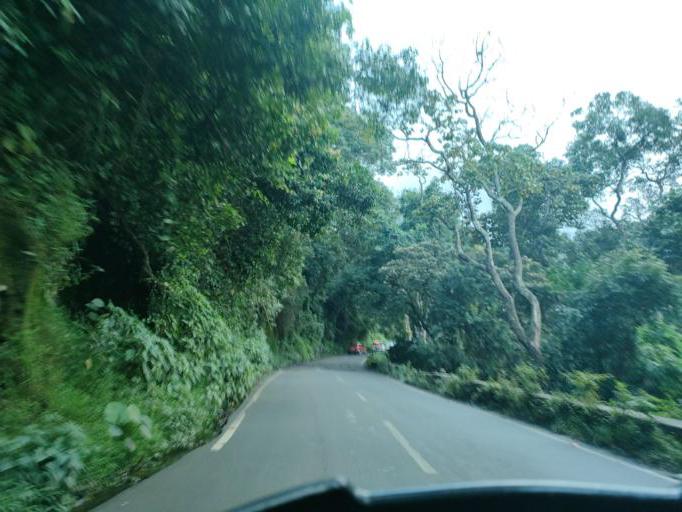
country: IN
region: Tamil Nadu
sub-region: Dindigul
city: Kodaikanal
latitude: 10.2546
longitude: 77.5263
